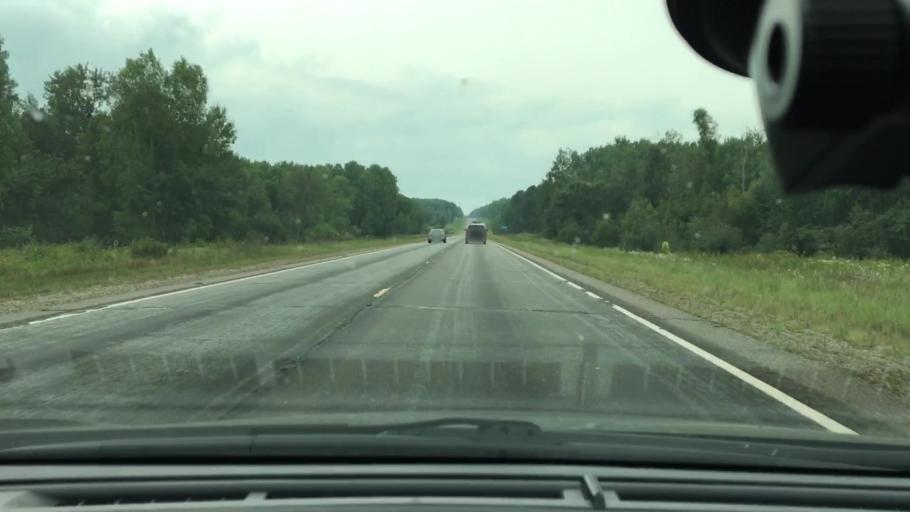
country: US
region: Minnesota
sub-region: Crow Wing County
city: Cross Lake
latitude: 46.6533
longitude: -93.9548
